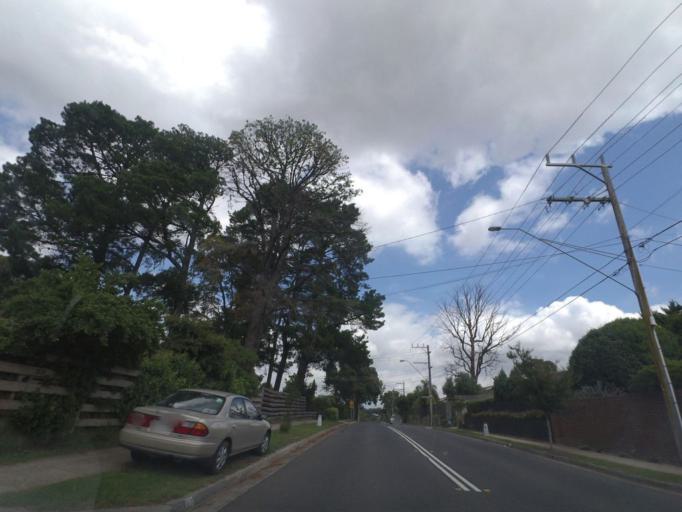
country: AU
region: Victoria
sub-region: Knox
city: Boronia
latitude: -37.8653
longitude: 145.2724
